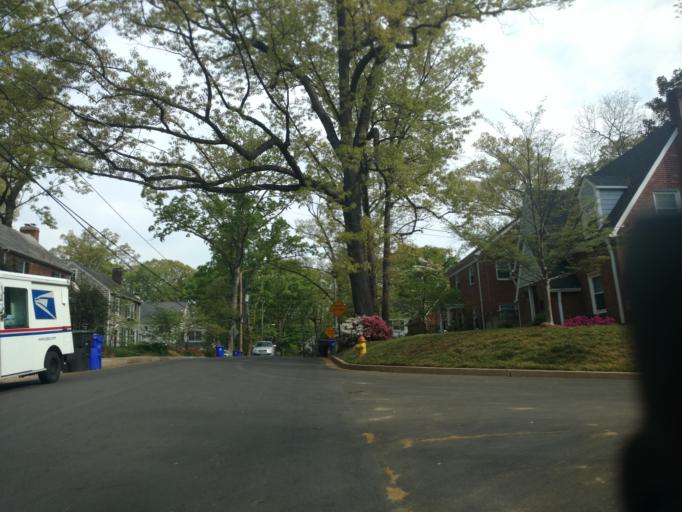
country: US
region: Virginia
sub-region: Arlington County
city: Arlington
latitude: 38.8836
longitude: -77.1295
